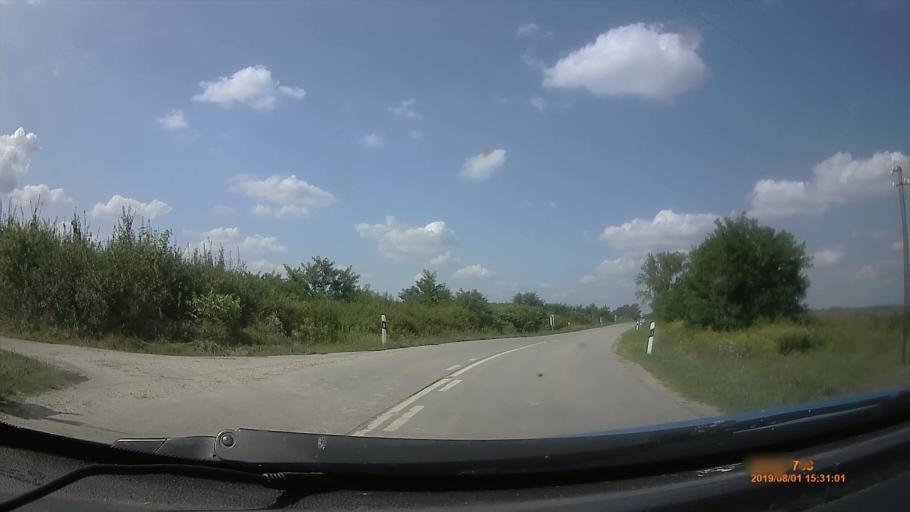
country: HU
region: Baranya
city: Sellye
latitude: 45.9347
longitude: 17.8661
